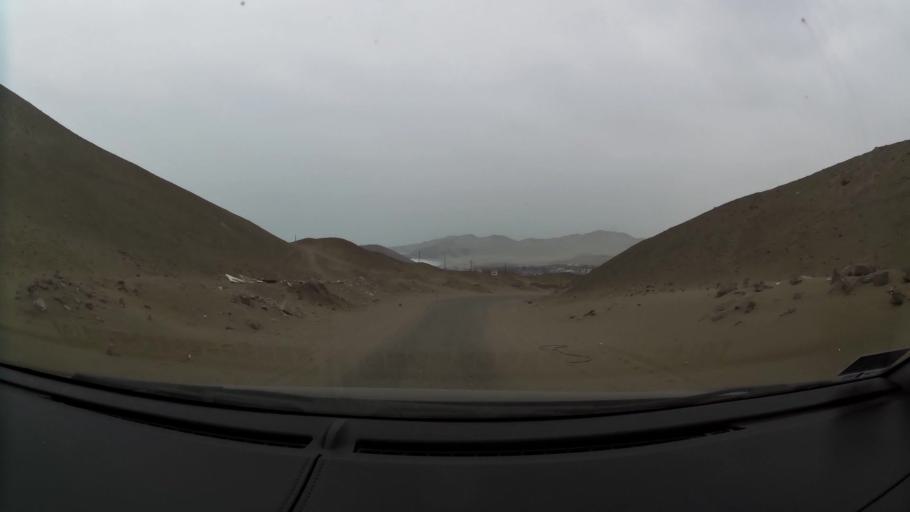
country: PE
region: Lima
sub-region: Lima
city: Santa Rosa
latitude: -11.8060
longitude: -77.1743
